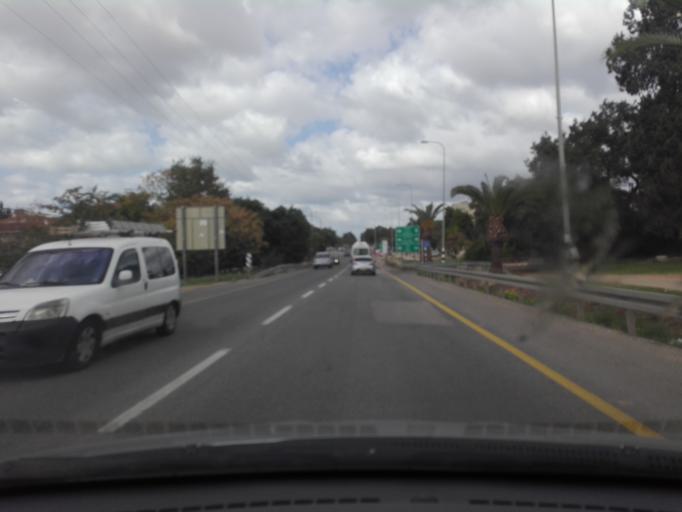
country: IL
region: Haifa
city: Hadera
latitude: 32.4739
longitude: 34.9777
